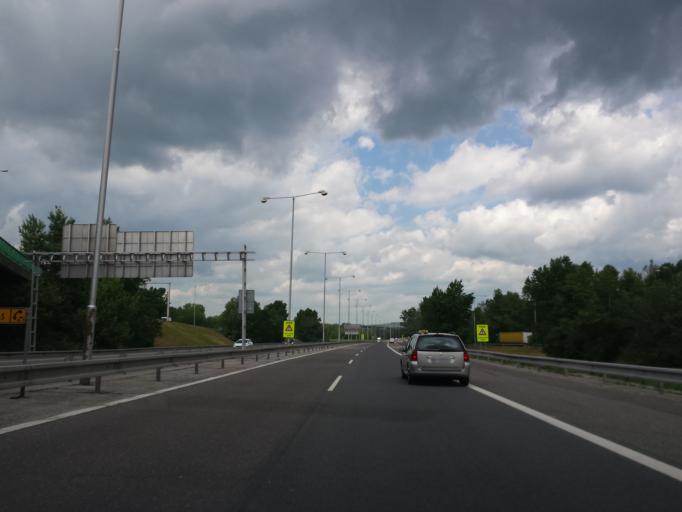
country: AT
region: Burgenland
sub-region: Politischer Bezirk Neusiedl am See
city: Kittsee
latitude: 48.1280
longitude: 17.0752
